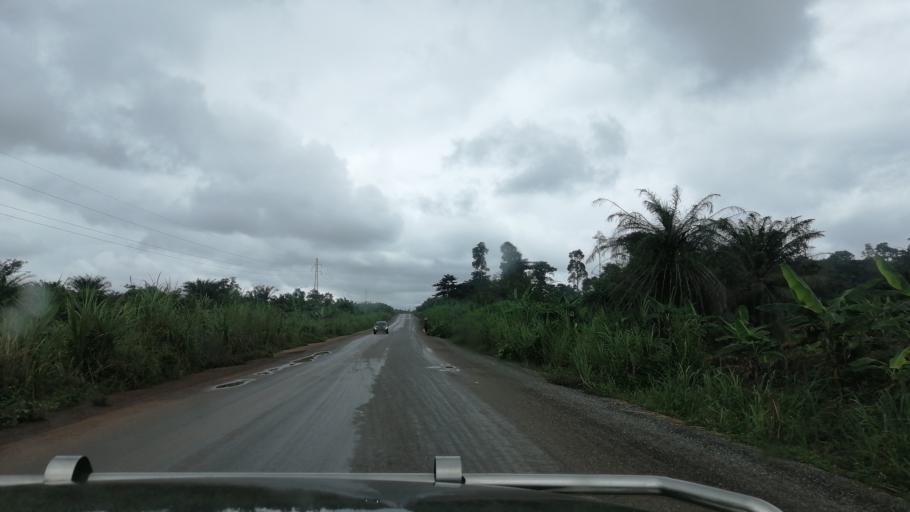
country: GH
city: Duayaw Nkwanta
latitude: 6.9041
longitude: -2.3989
